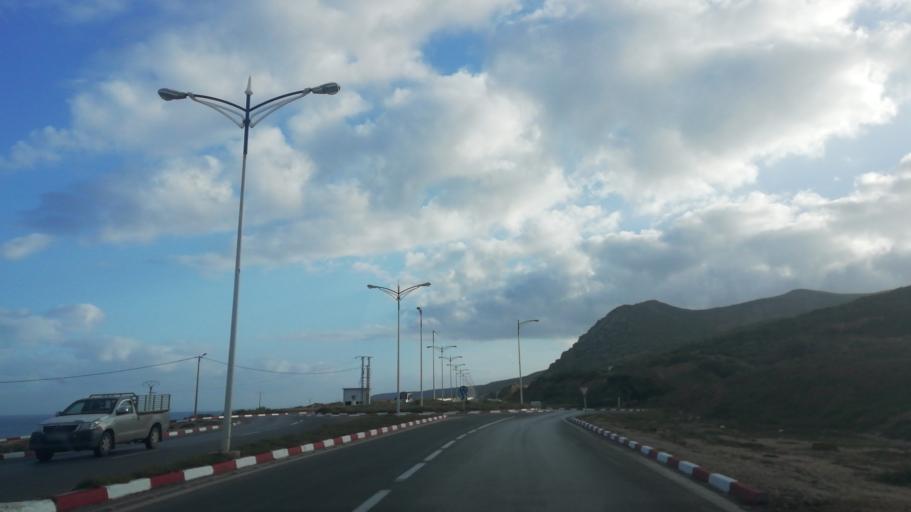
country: DZ
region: Mostaganem
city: Mostaganem
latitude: 36.0517
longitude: 0.1533
